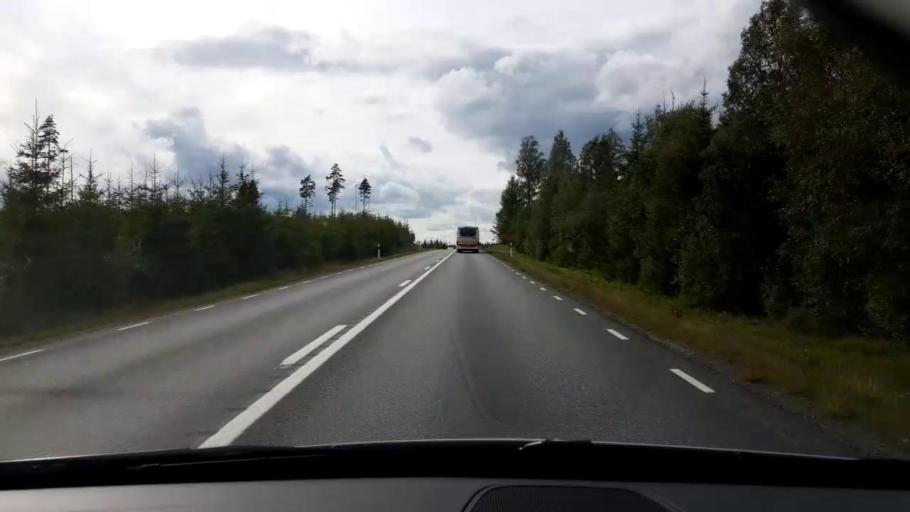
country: SE
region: Joenkoeping
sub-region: Savsjo Kommun
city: Saevsjoe
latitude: 57.3929
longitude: 14.7240
